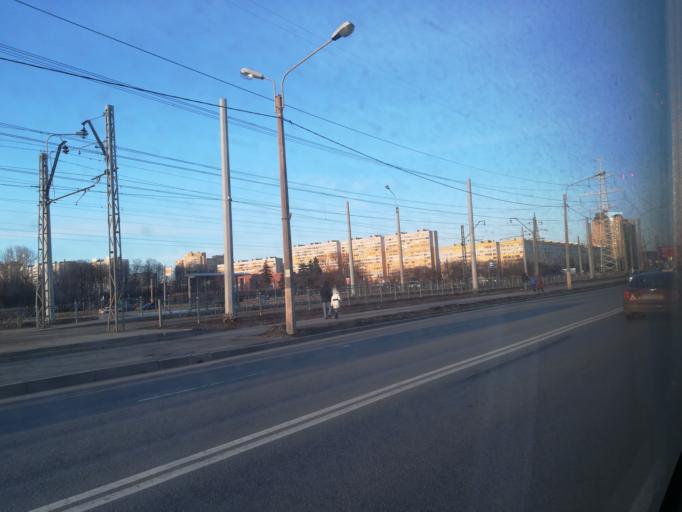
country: RU
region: St.-Petersburg
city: Uritsk
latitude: 59.8464
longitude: 30.1716
